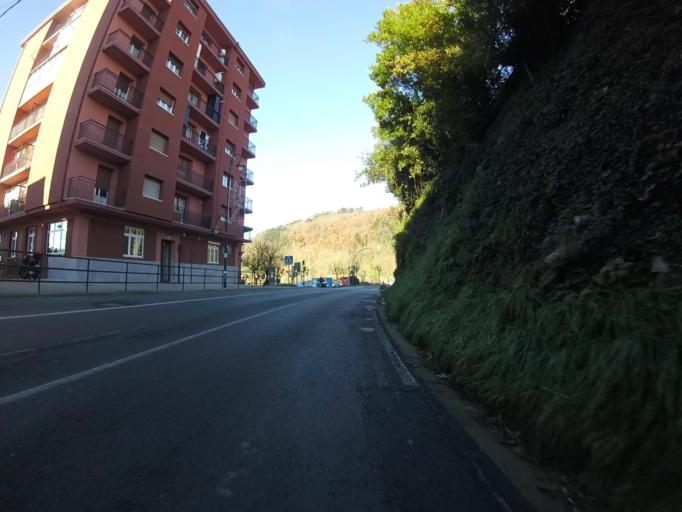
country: ES
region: Basque Country
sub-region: Provincia de Guipuzcoa
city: Lezo
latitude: 43.3226
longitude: -1.9003
